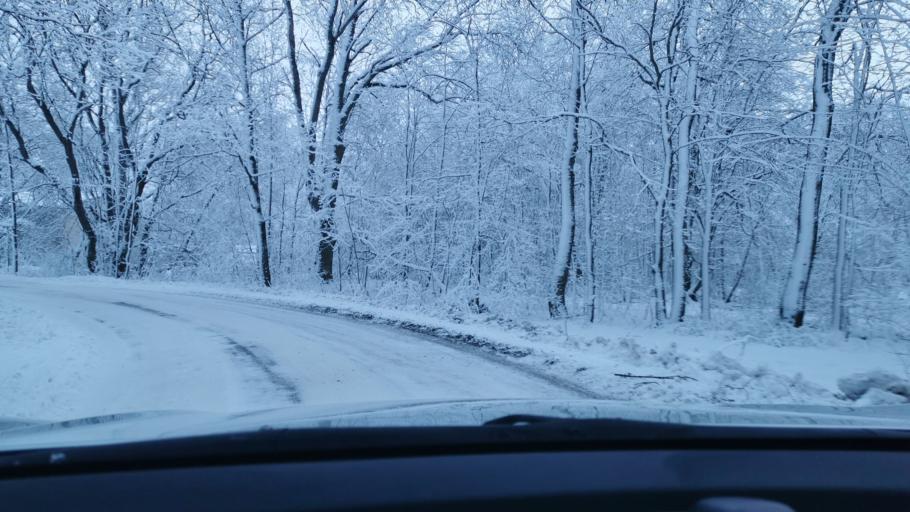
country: EE
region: Laeaene-Virumaa
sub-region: Haljala vald
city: Haljala
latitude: 59.4693
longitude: 26.3430
